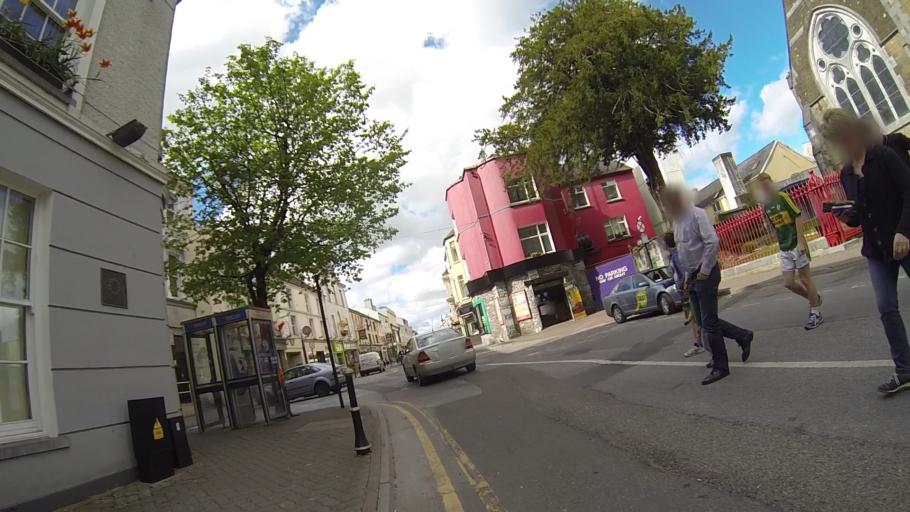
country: IE
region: Munster
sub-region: Ciarrai
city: Cill Airne
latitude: 52.0580
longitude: -9.5086
